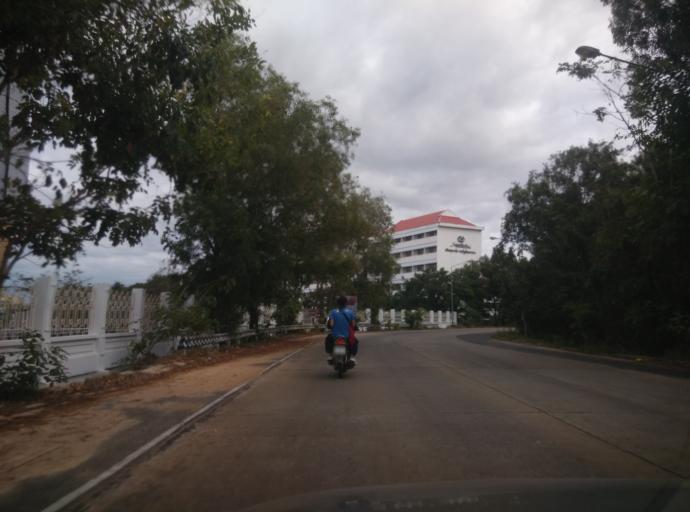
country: TH
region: Sisaket
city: Si Sa Ket
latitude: 15.1181
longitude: 104.3547
